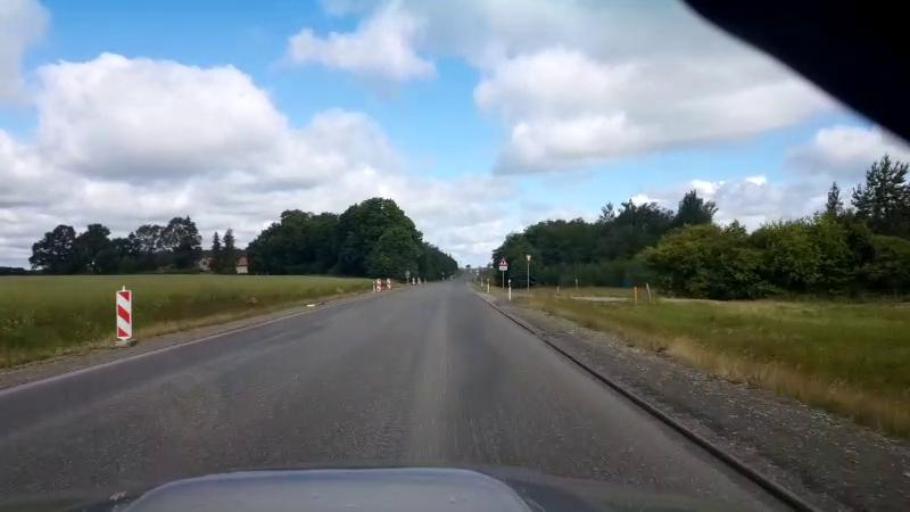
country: LV
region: Bauskas Rajons
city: Bauska
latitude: 56.3264
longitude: 24.3083
